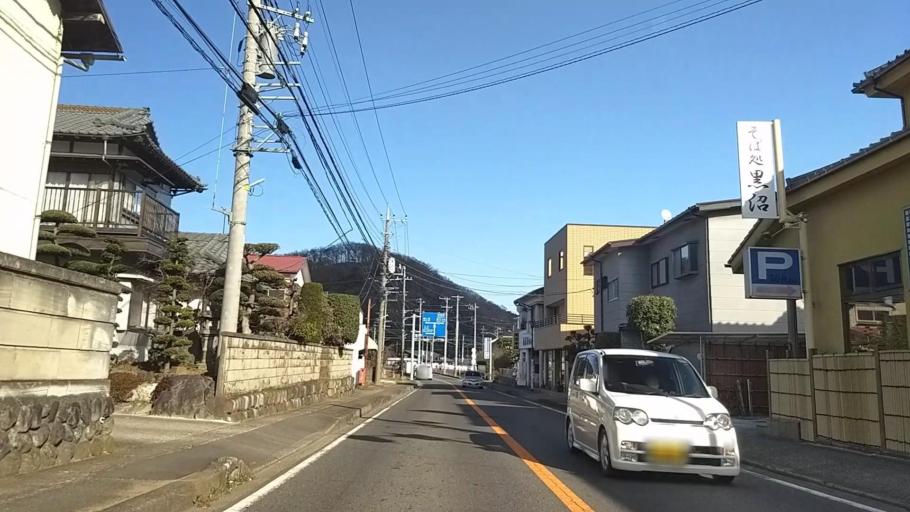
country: JP
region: Kanagawa
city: Isehara
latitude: 35.4334
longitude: 139.3149
